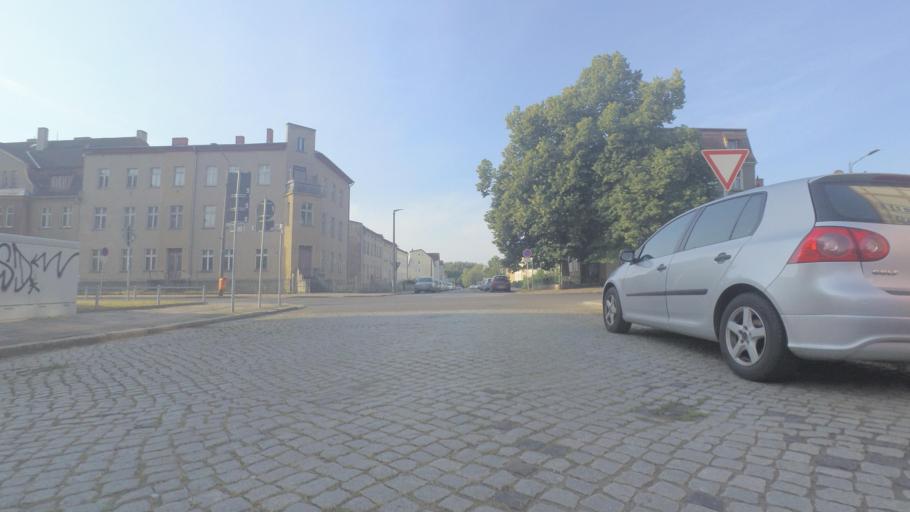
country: DE
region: Mecklenburg-Vorpommern
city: Demmin
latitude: 53.9028
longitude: 13.0461
